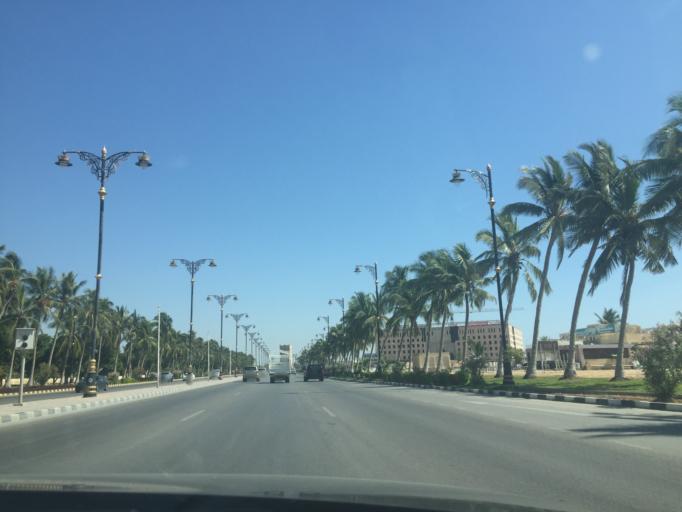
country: OM
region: Zufar
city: Salalah
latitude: 17.0235
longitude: 54.1056
